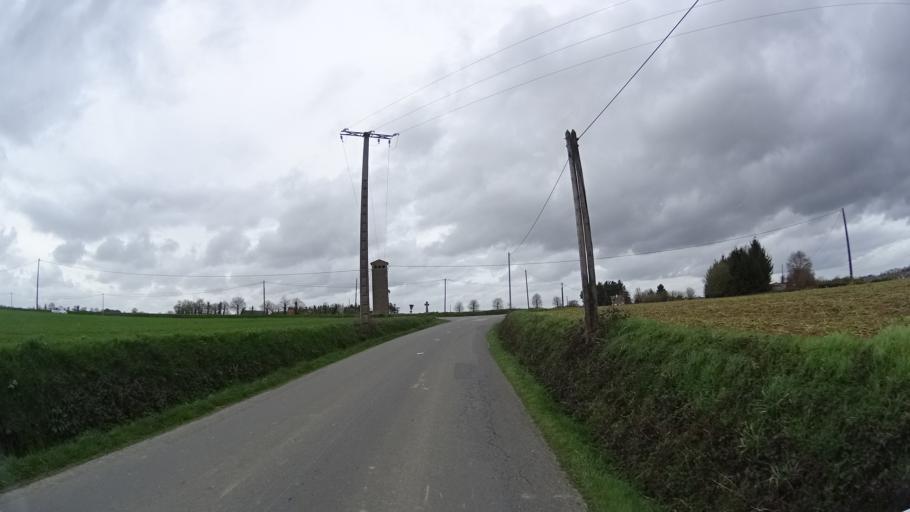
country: FR
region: Brittany
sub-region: Departement d'Ille-et-Vilaine
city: Saint-Gilles
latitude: 48.1839
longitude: -1.8336
